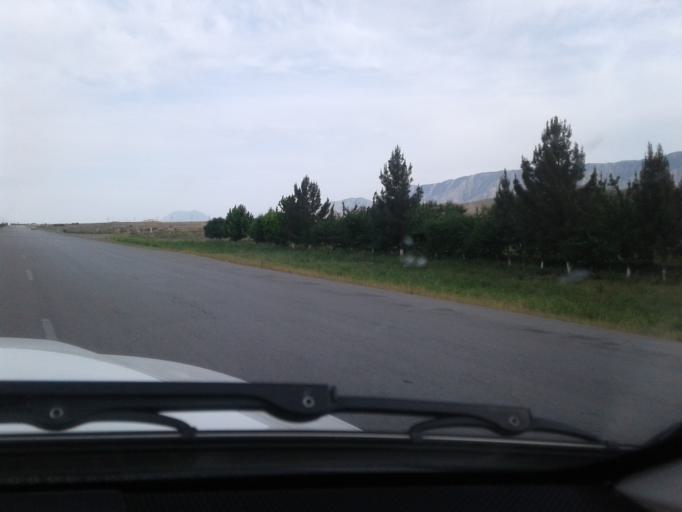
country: TM
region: Ahal
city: Baharly
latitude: 38.2410
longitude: 57.7664
